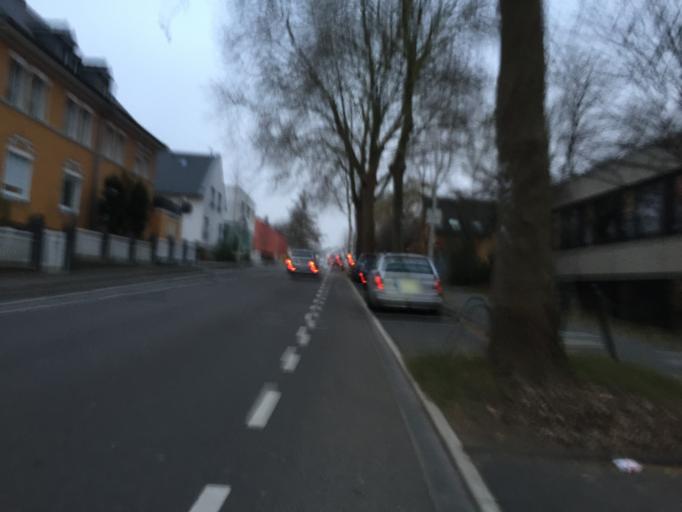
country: DE
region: North Rhine-Westphalia
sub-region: Regierungsbezirk Koln
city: Bonn
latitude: 50.7336
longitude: 7.0671
